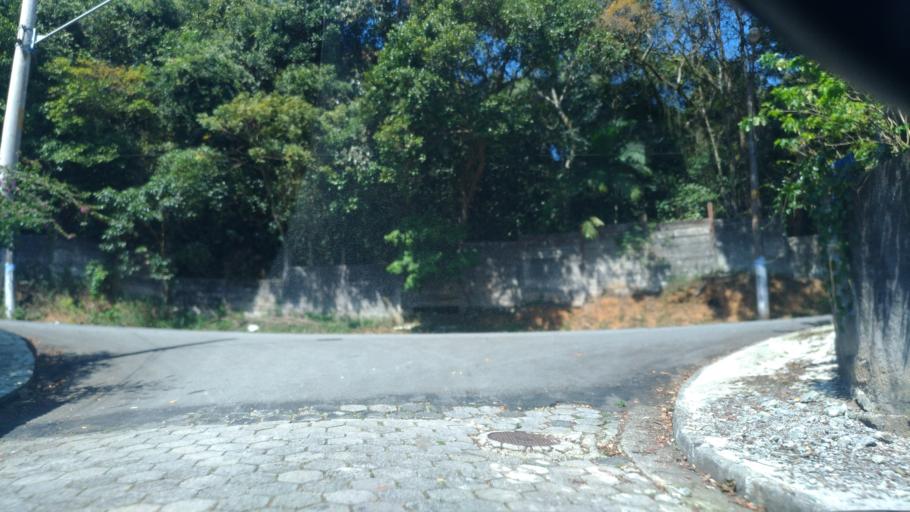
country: BR
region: Sao Paulo
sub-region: Sao Bernardo Do Campo
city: Sao Bernardo do Campo
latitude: -23.7736
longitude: -46.5198
